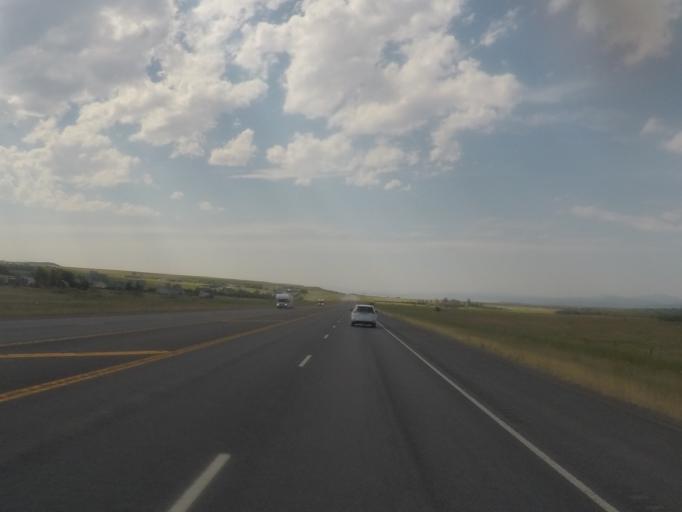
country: US
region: Montana
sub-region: Lewis and Clark County
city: East Helena
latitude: 46.5408
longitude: -111.7371
